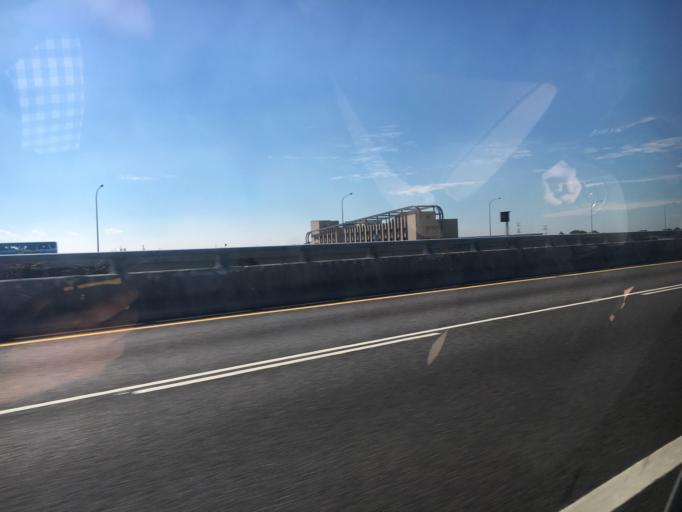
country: TW
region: Taiwan
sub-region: Taoyuan
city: Taoyuan
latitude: 25.0656
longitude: 121.3545
